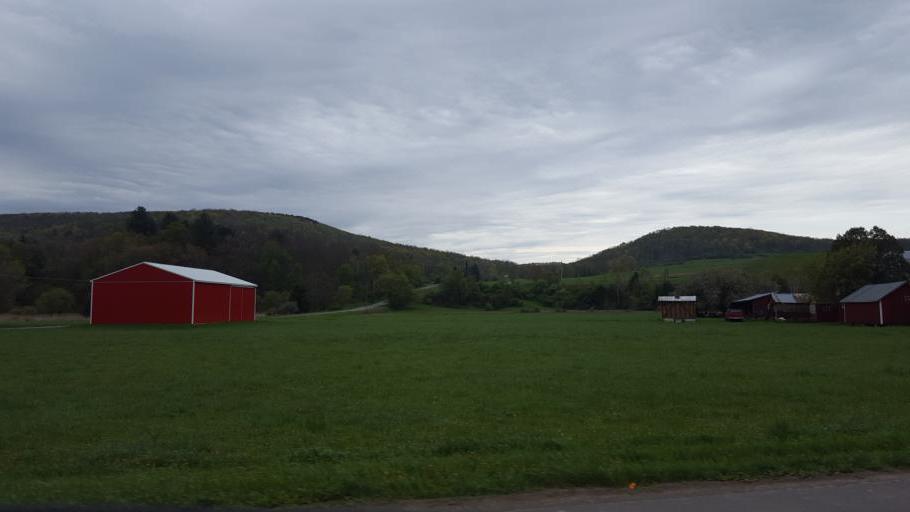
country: US
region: Pennsylvania
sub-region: Tioga County
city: Westfield
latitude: 41.9245
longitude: -77.5257
